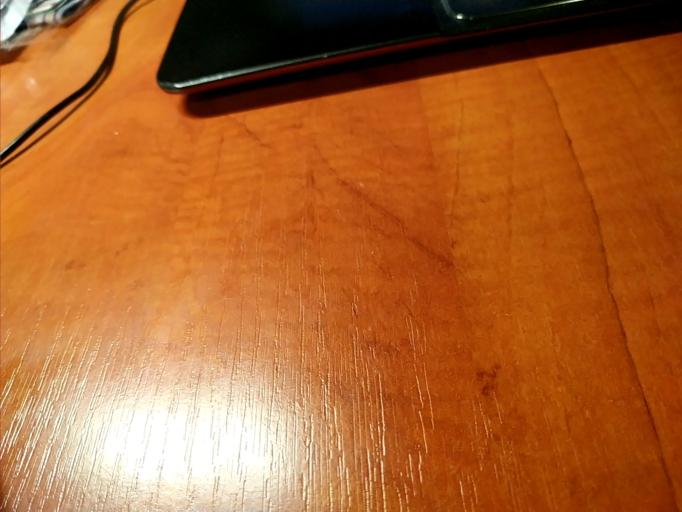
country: RU
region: Tverskaya
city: Ves'yegonsk
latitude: 58.8012
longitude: 37.5436
